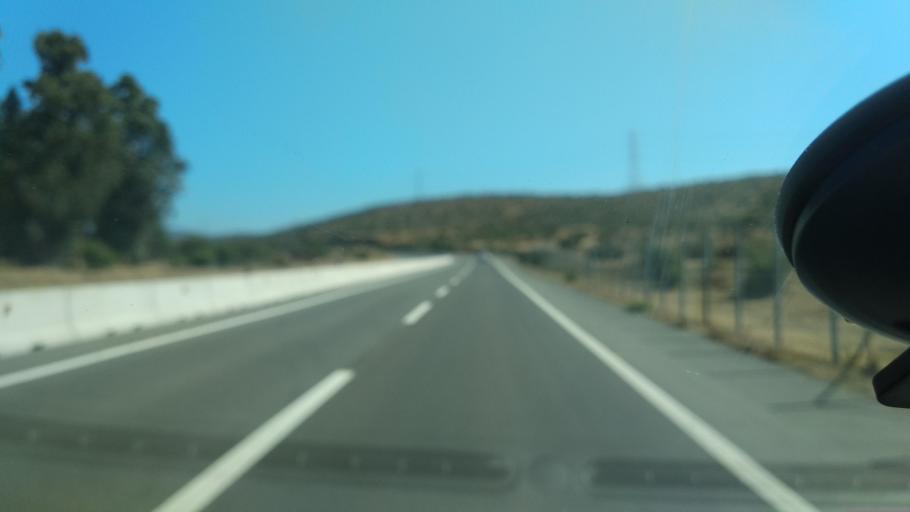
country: CL
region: Valparaiso
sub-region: Provincia de Marga Marga
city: Villa Alemana
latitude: -32.9933
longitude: -71.3291
